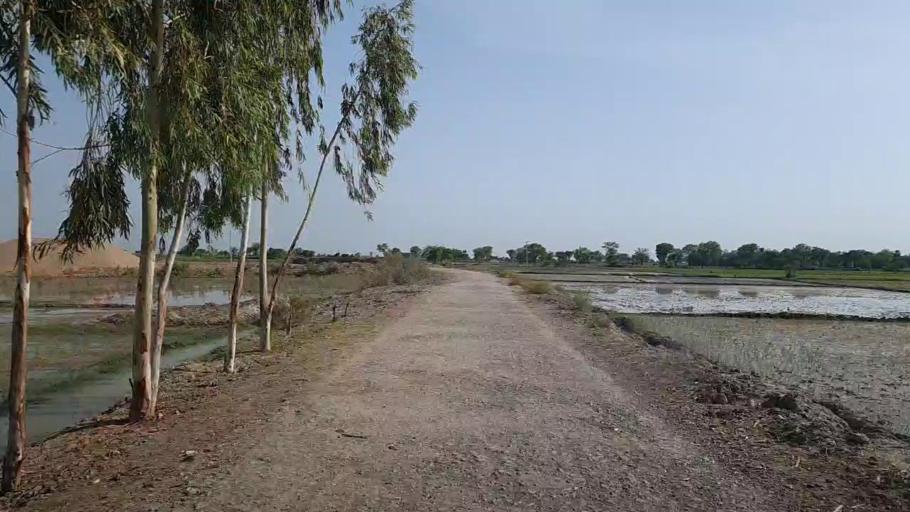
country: PK
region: Sindh
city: Sita Road
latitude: 27.0901
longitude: 67.8485
